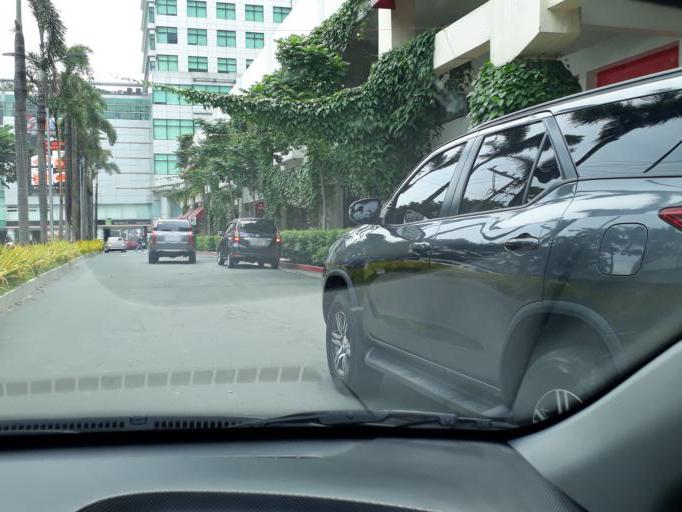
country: PH
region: Metro Manila
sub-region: Quezon City
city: Quezon City
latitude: 14.6224
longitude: 121.0545
